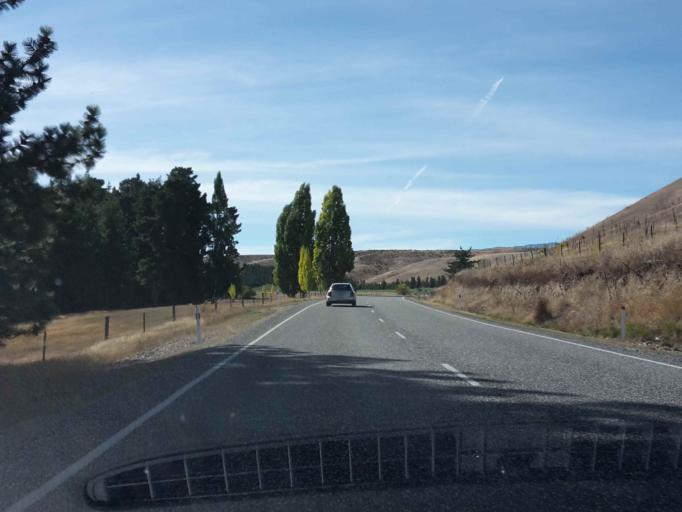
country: NZ
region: Otago
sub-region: Queenstown-Lakes District
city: Wanaka
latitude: -44.8037
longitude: 169.4682
